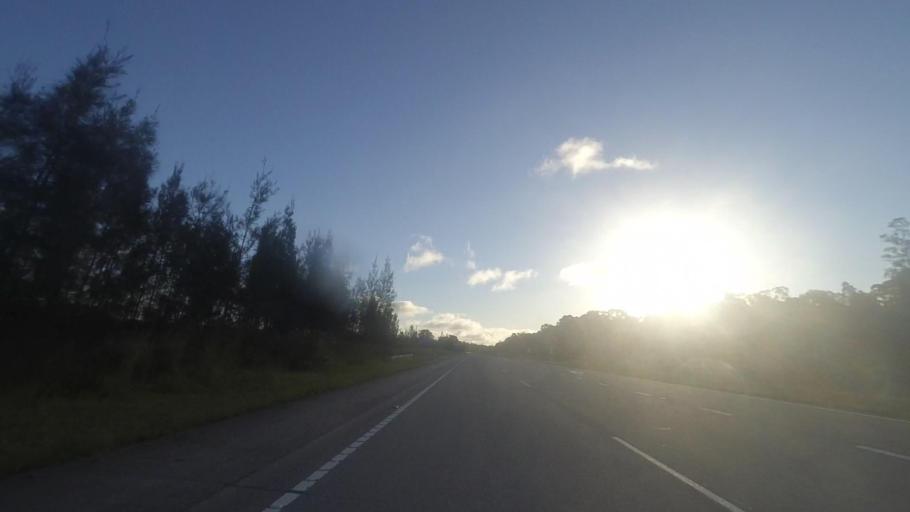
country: AU
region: New South Wales
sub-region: Great Lakes
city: Hawks Nest
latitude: -32.5404
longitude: 152.1677
